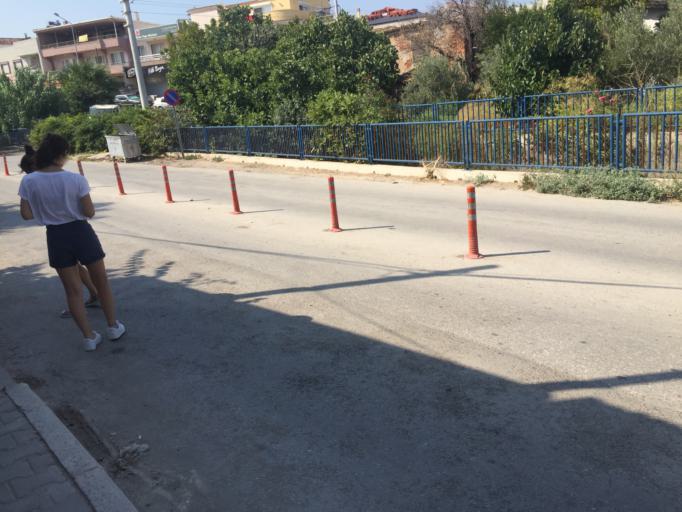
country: TR
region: Izmir
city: Urla
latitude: 38.3246
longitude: 26.7645
